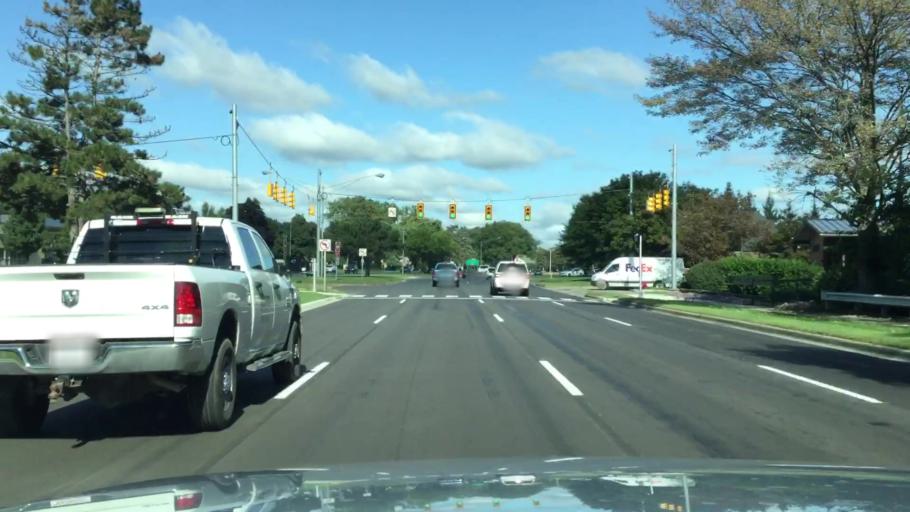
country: US
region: Michigan
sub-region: Oakland County
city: Birmingham
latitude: 42.5539
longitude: -83.2180
